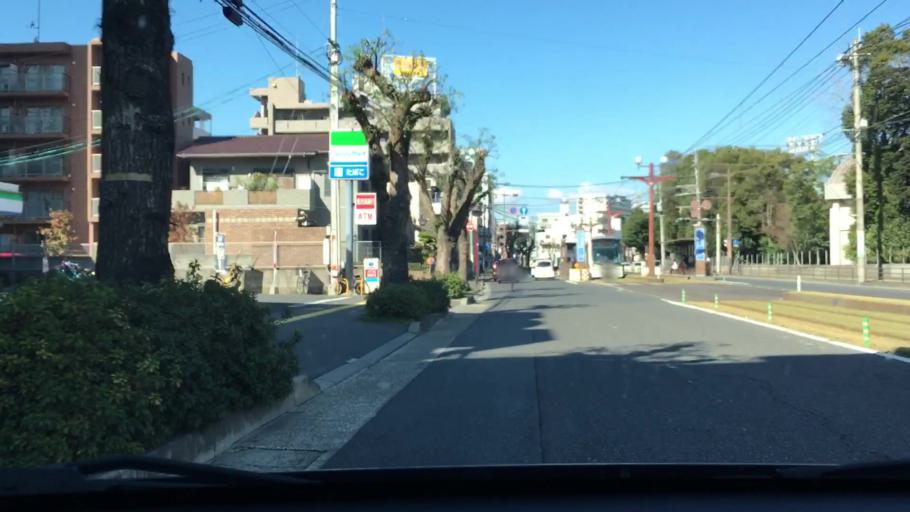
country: JP
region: Kagoshima
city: Kagoshima-shi
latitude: 31.5661
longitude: 130.5432
